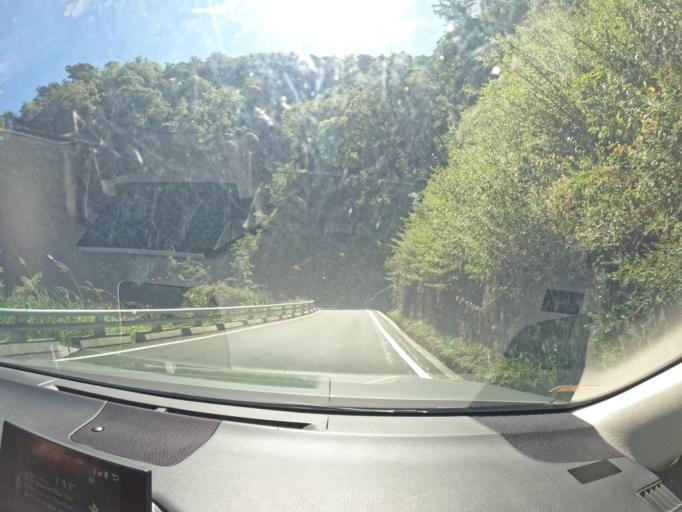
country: TW
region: Taiwan
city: Yujing
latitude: 23.2834
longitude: 120.8864
